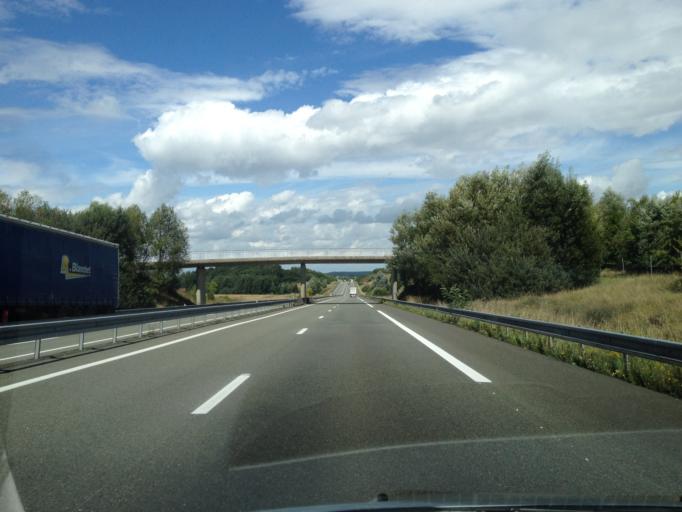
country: FR
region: Pays de la Loire
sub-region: Departement de la Sarthe
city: Sainte-Jamme-sur-Sarthe
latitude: 48.1376
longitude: 0.1437
